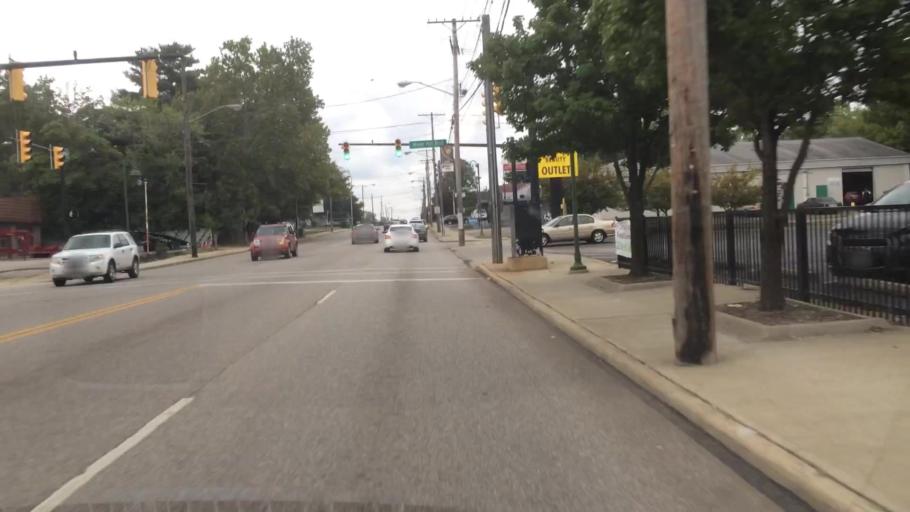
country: US
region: Ohio
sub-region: Cuyahoga County
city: Maple Heights
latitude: 41.4162
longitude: -81.5711
